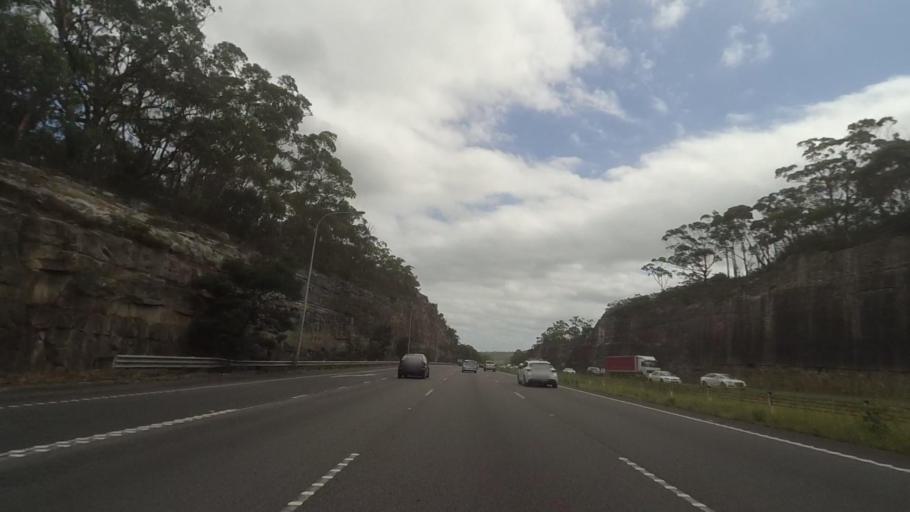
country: AU
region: New South Wales
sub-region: Gosford Shire
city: Point Clare
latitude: -33.4305
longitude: 151.2241
